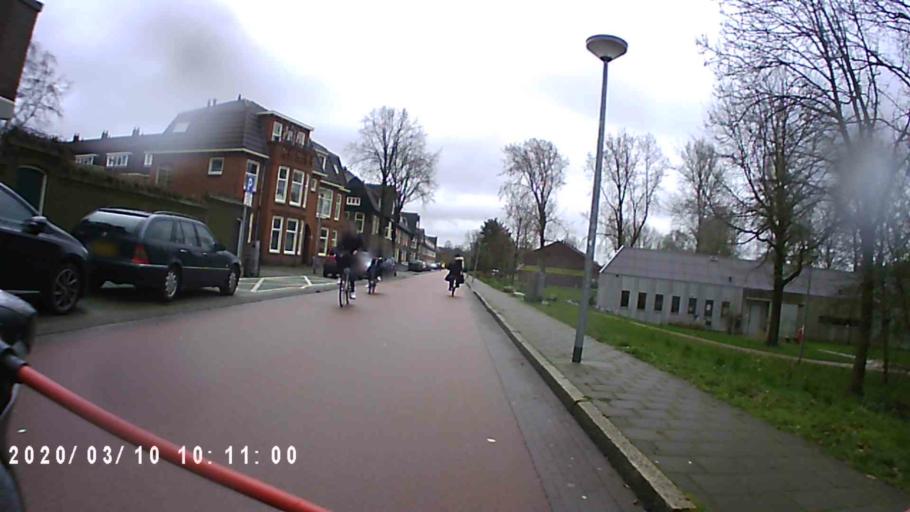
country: NL
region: Groningen
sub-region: Gemeente Groningen
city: Korrewegwijk
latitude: 53.2286
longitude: 6.5492
